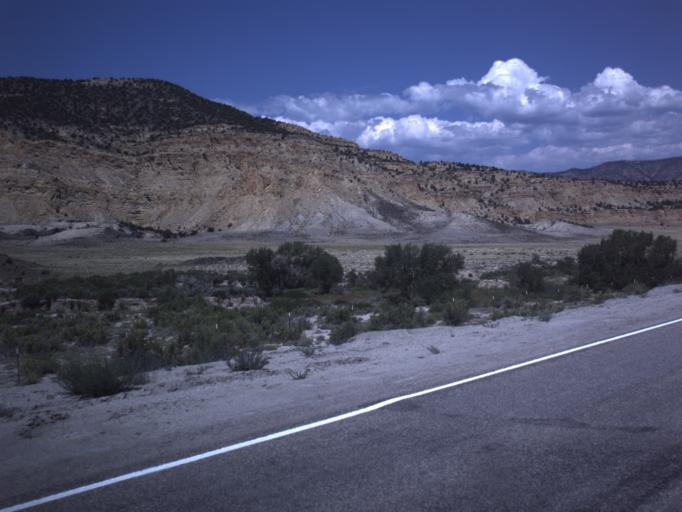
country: US
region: Utah
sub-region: Emery County
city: Ferron
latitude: 38.7810
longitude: -111.3503
